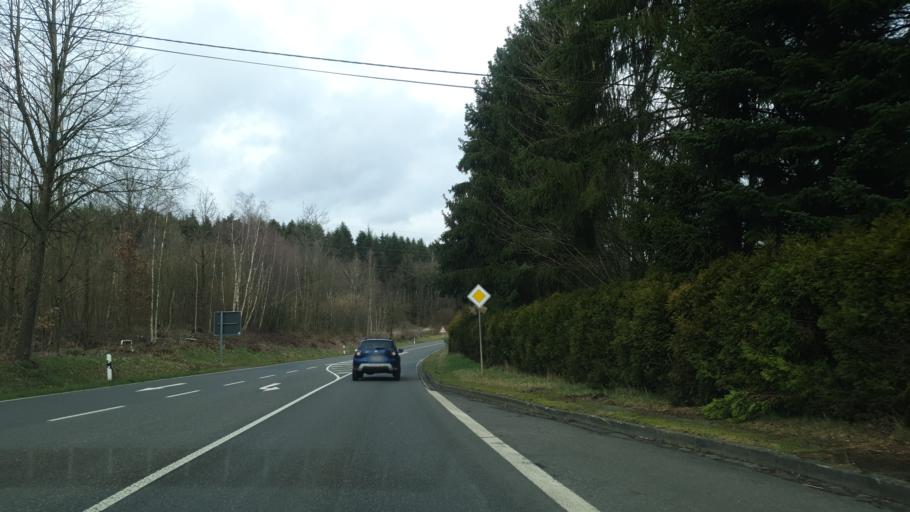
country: DE
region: Rheinland-Pfalz
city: Niederhofen
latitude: 50.5737
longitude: 7.5883
